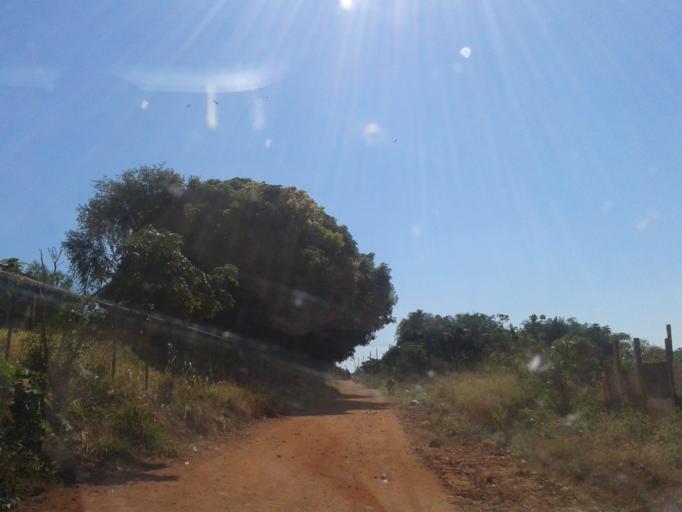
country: BR
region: Minas Gerais
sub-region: Ituiutaba
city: Ituiutaba
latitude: -19.0060
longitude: -49.4789
